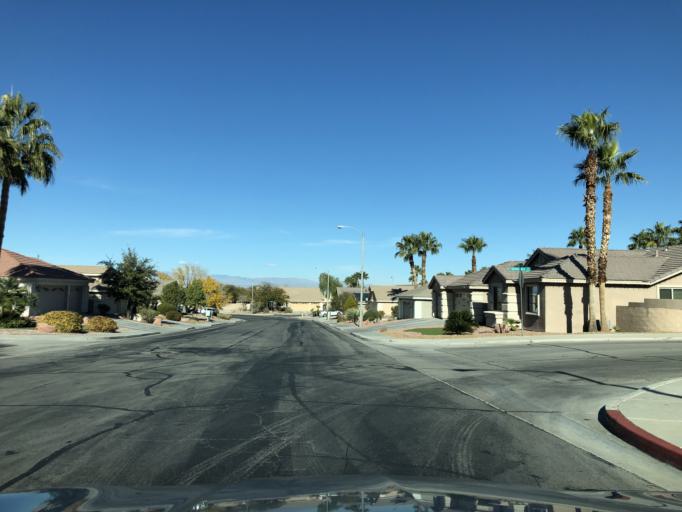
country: US
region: Nevada
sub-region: Clark County
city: Whitney
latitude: 36.0079
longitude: -115.0899
